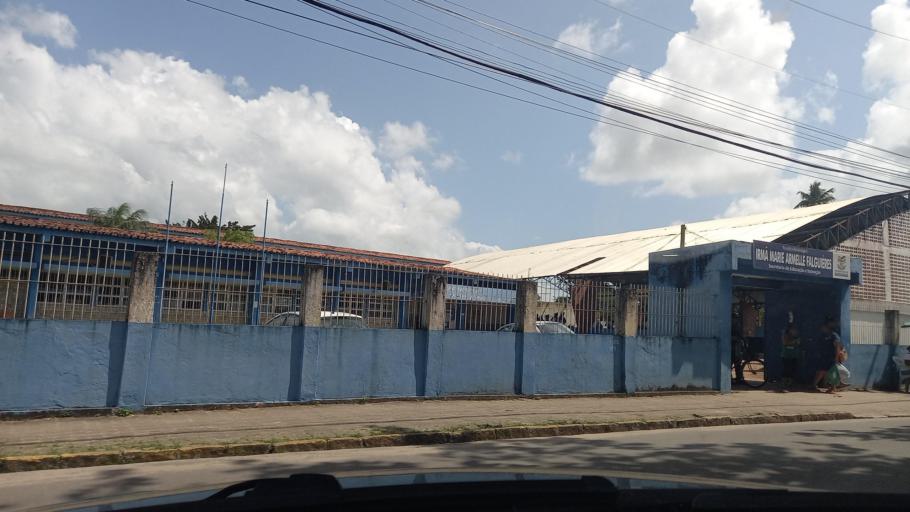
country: BR
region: Pernambuco
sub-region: Goiana
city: Goiana
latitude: -7.5636
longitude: -35.0000
